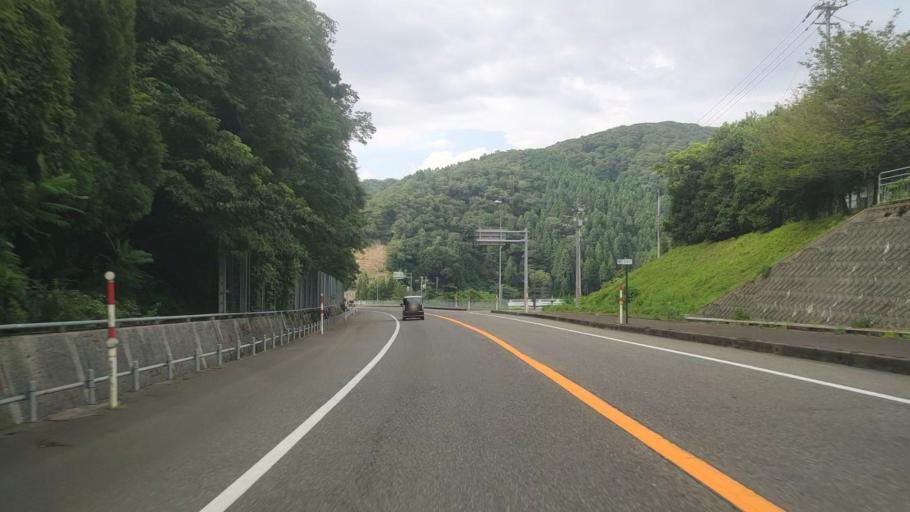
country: JP
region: Fukui
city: Takefu
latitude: 35.8147
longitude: 136.1014
